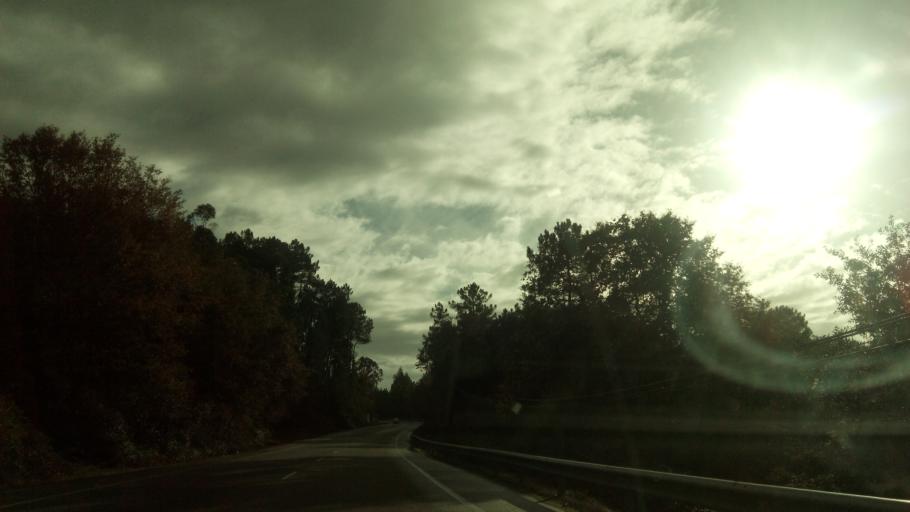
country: ES
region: Galicia
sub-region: Provincia de Pontevedra
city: Ponteareas
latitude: 42.2017
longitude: -8.5098
